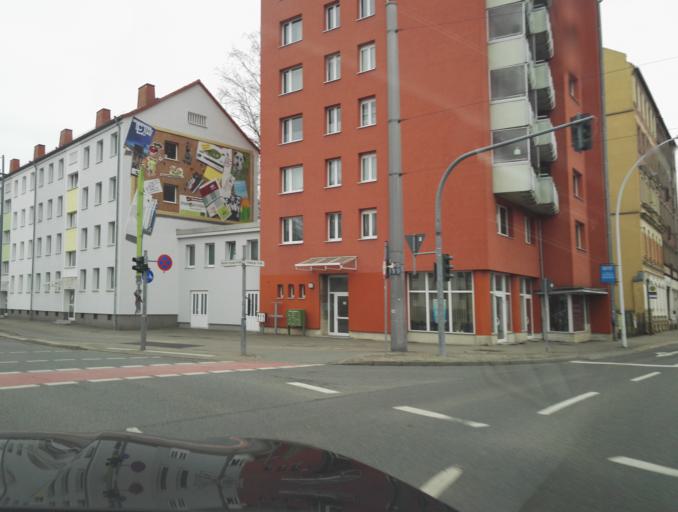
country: DE
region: Saxony
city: Chemnitz
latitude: 50.8252
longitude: 12.9205
